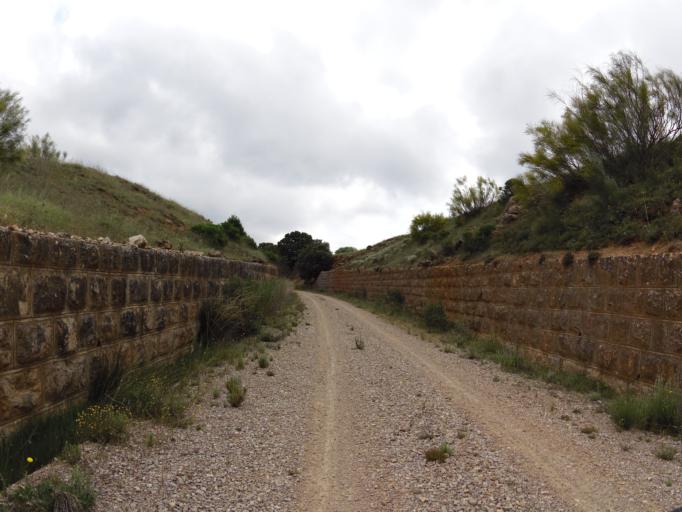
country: ES
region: Castille-La Mancha
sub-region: Provincia de Albacete
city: Robledo
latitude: 38.7310
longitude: -2.4693
